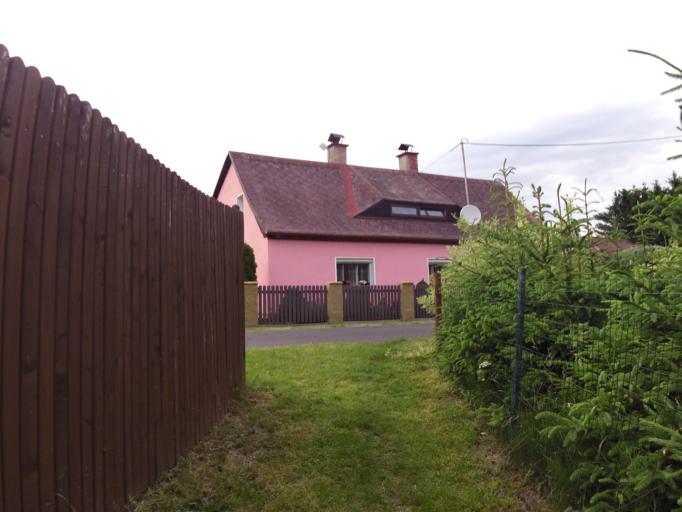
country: CZ
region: Ustecky
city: Varnsdorf
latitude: 50.8964
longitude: 14.6173
